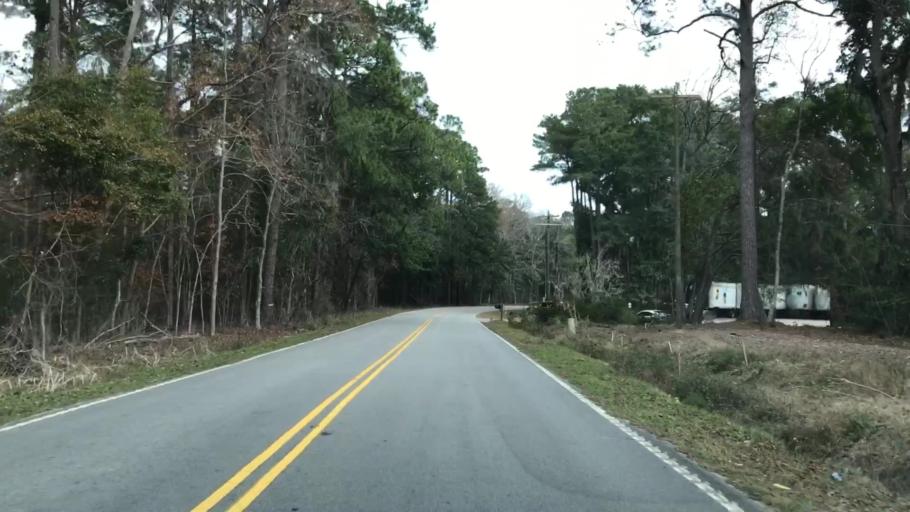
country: US
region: South Carolina
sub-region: Beaufort County
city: Burton
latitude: 32.4180
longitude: -80.7413
